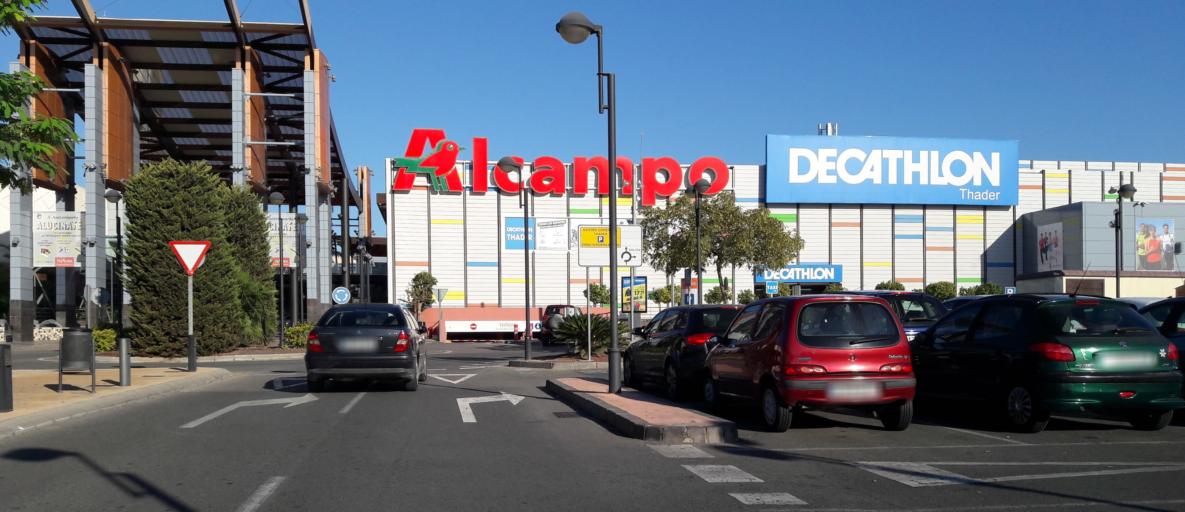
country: ES
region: Murcia
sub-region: Murcia
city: Murcia
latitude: 38.0312
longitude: -1.1479
